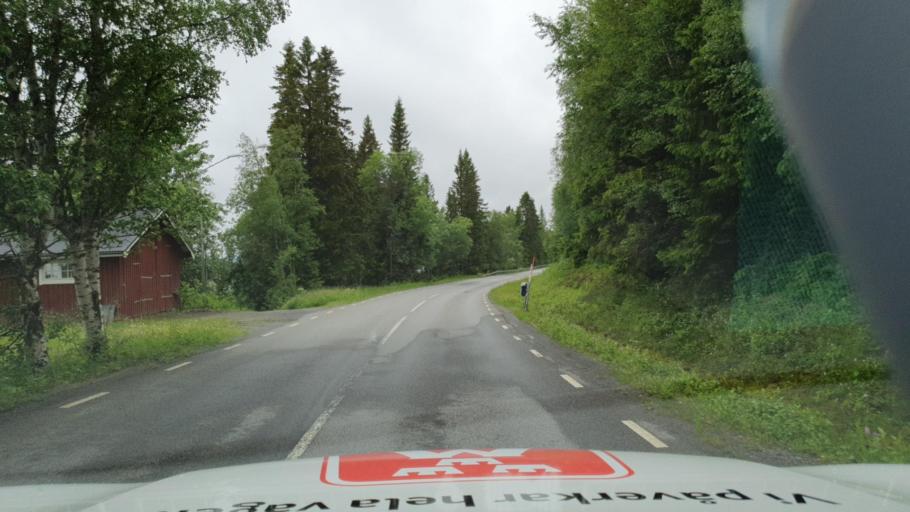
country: SE
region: Jaemtland
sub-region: Are Kommun
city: Are
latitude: 63.5022
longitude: 13.1603
